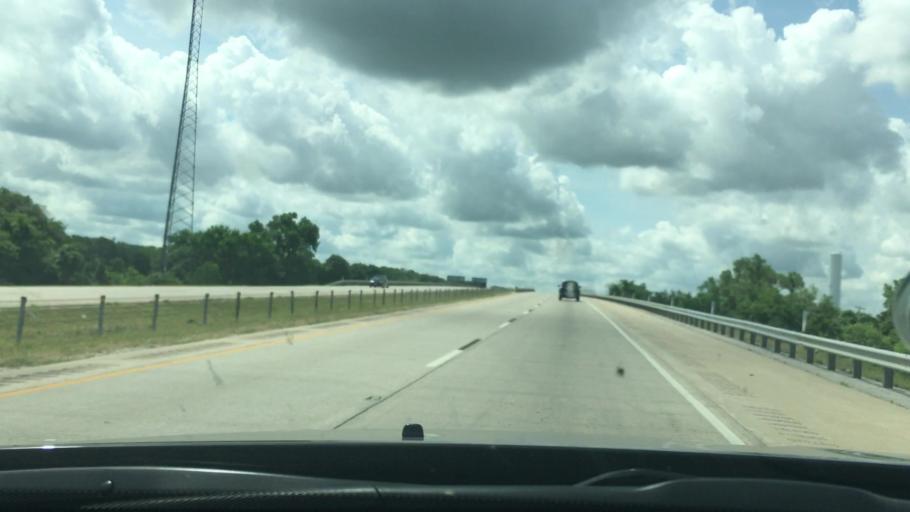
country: US
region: Oklahoma
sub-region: Love County
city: Marietta
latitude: 33.8385
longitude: -97.1329
